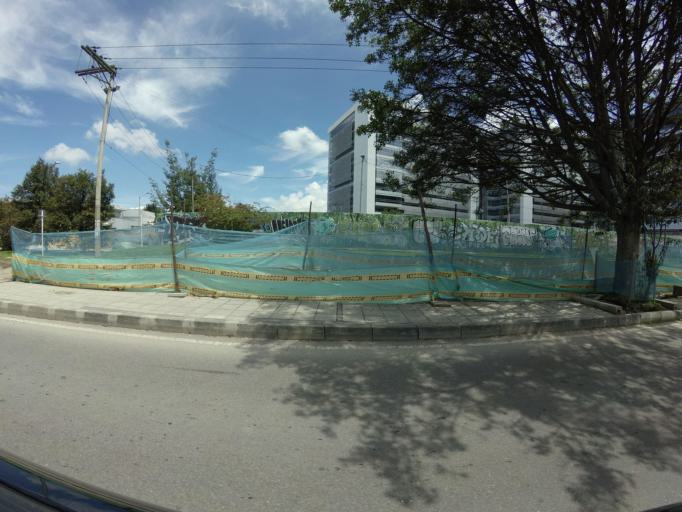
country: CO
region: Bogota D.C.
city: Barrio San Luis
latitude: 4.7076
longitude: -74.0640
